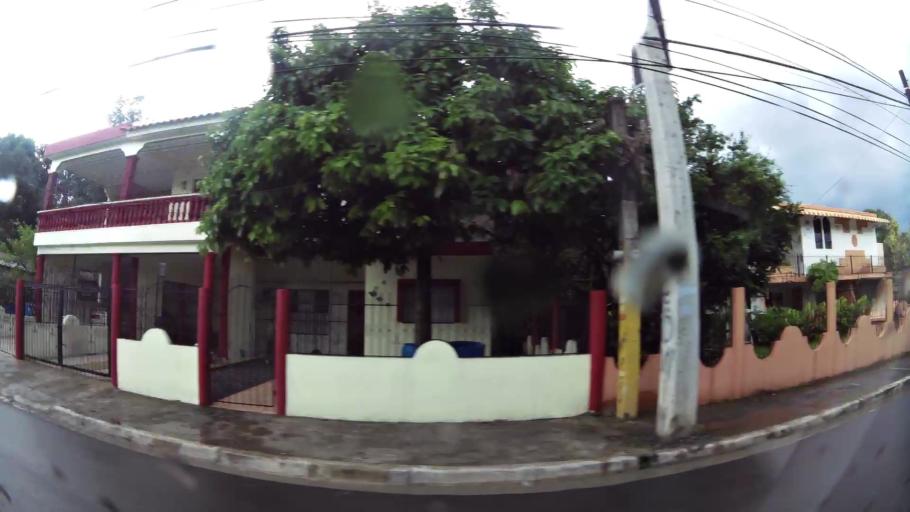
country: DO
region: Monsenor Nouel
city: Bonao
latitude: 18.9379
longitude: -70.4000
